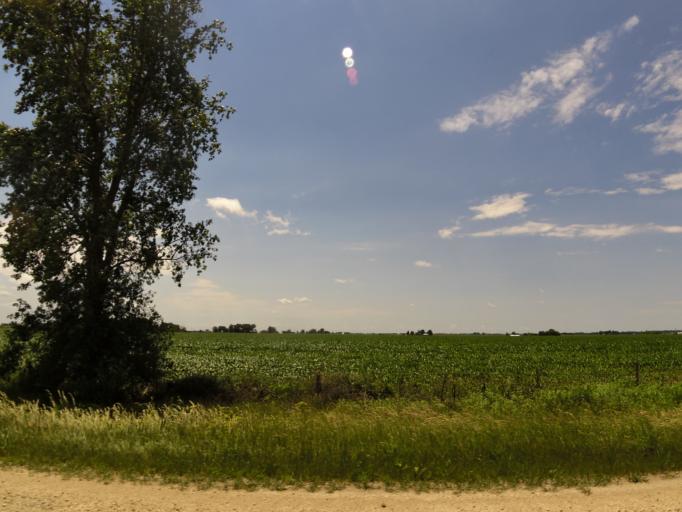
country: US
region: Iowa
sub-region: Buchanan County
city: Fairbank
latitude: 42.7146
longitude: -92.1061
